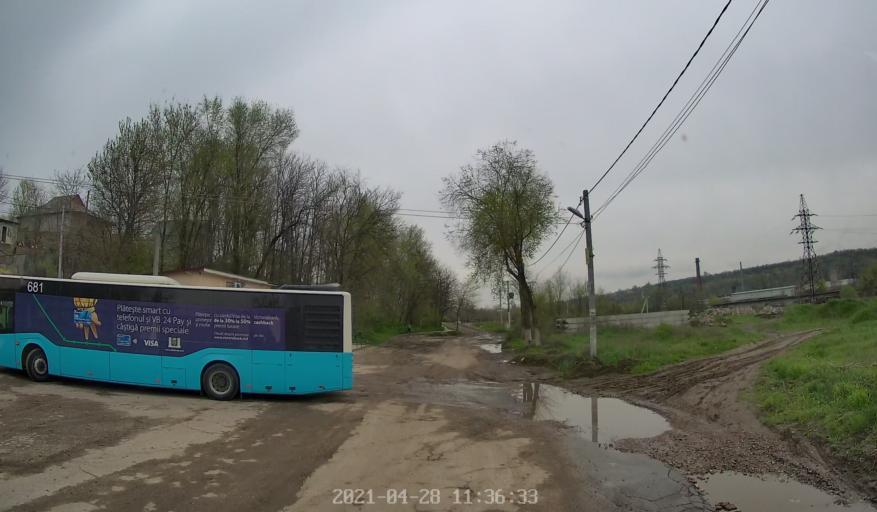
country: MD
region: Chisinau
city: Singera
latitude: 46.9443
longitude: 28.9499
